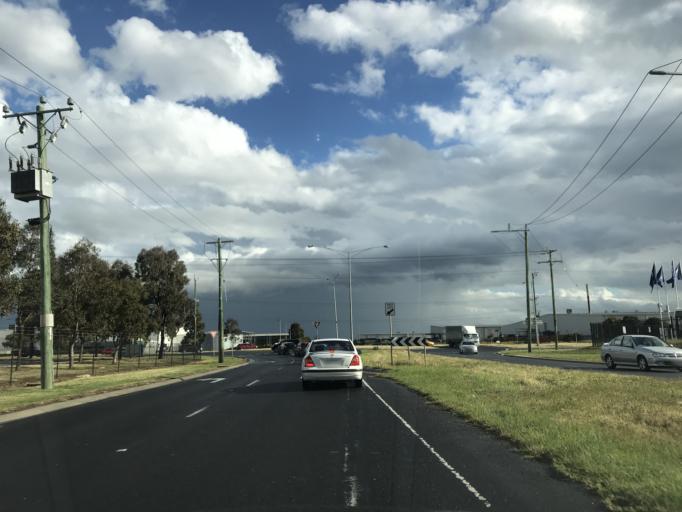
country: AU
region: Victoria
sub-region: Brimbank
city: Derrimut
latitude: -37.8111
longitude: 144.7692
